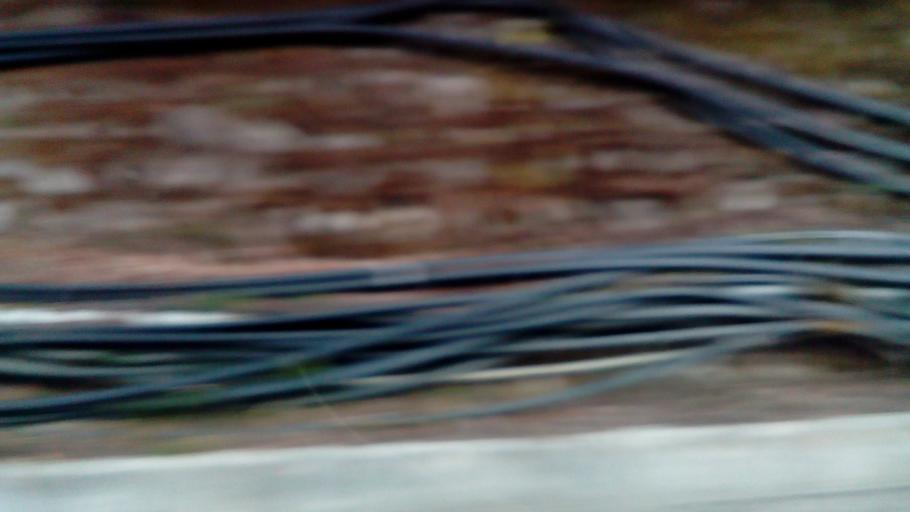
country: TW
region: Taiwan
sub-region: Nantou
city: Puli
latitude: 24.2662
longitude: 121.2604
